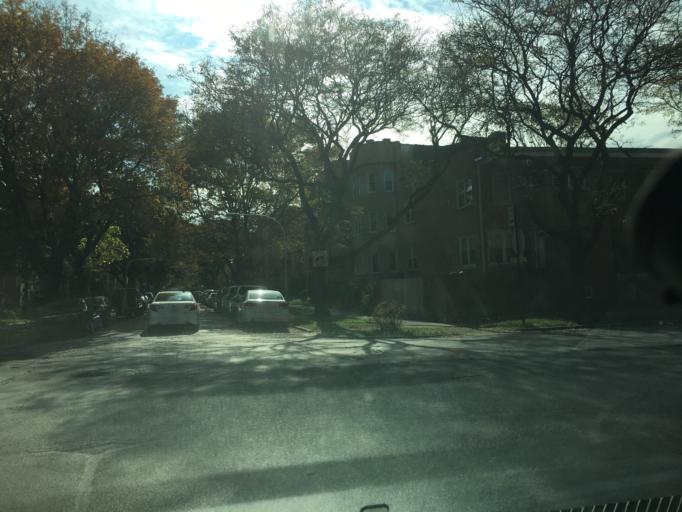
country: US
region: Illinois
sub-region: Cook County
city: Lincolnwood
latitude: 41.9942
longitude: -87.6971
